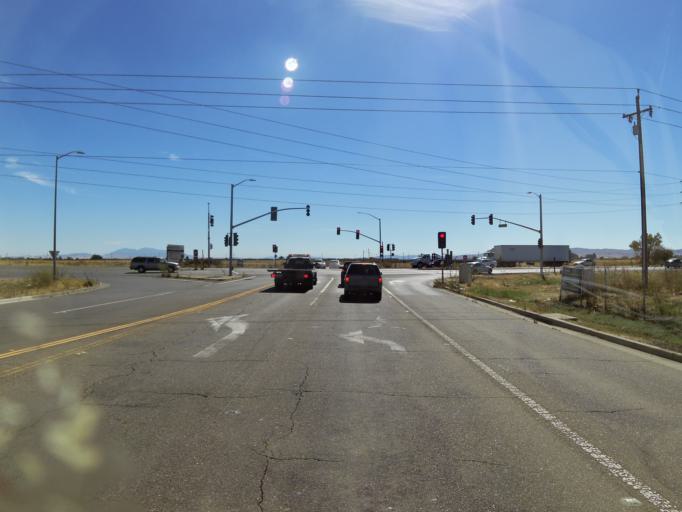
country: US
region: California
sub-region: Solano County
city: Suisun
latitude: 38.2419
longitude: -122.0504
